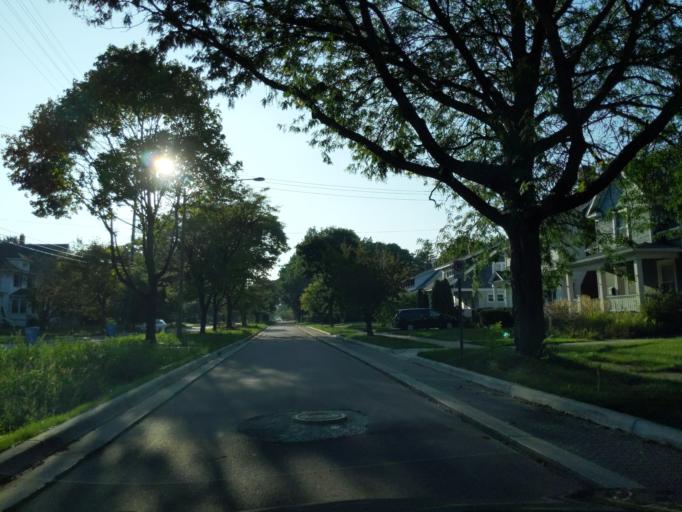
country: US
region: Michigan
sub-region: Ingham County
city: Lansing
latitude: 42.7150
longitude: -84.5589
